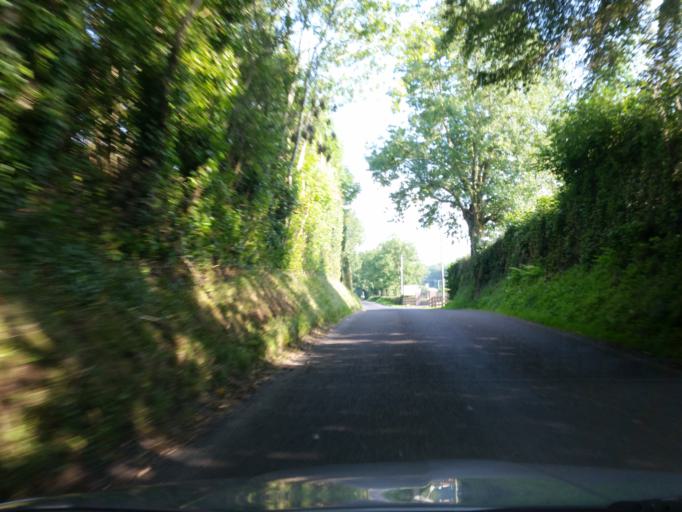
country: GB
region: Northern Ireland
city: Lisnaskea
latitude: 54.2875
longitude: -7.4436
